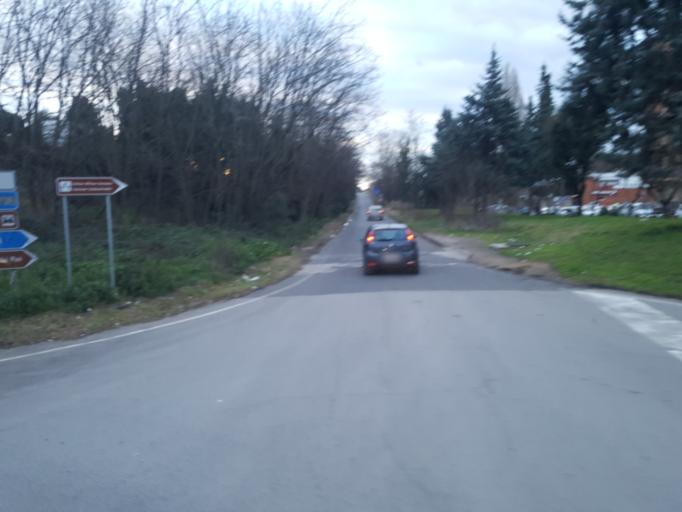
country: IT
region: Latium
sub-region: Citta metropolitana di Roma Capitale
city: Area Produttiva
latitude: 41.6731
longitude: 12.5034
